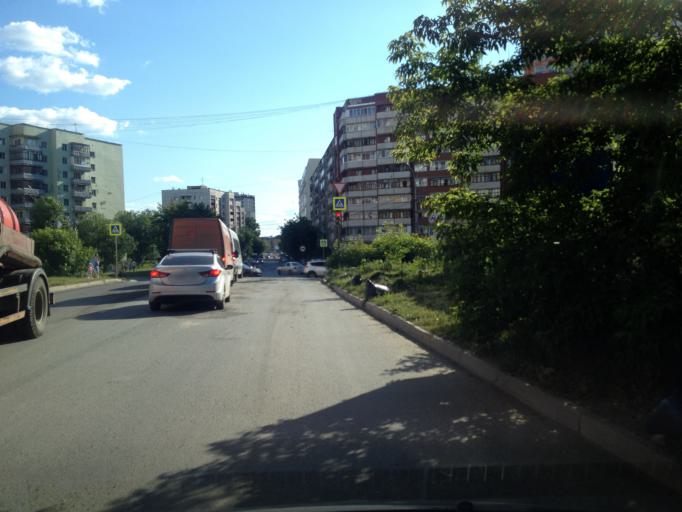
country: RU
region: Sverdlovsk
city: Yekaterinburg
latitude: 56.9082
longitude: 60.6210
